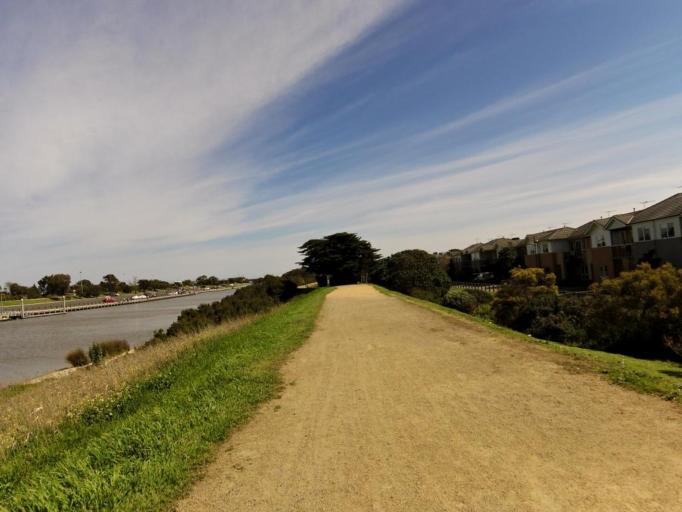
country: AU
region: Victoria
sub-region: Kingston
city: Bonbeach
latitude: -38.0689
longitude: 145.1317
